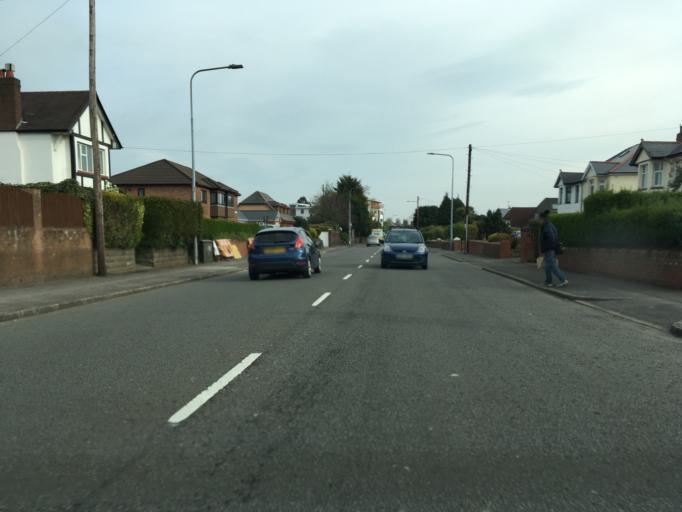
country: GB
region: Wales
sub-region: Cardiff
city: Radyr
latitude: 51.5199
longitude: -3.2098
